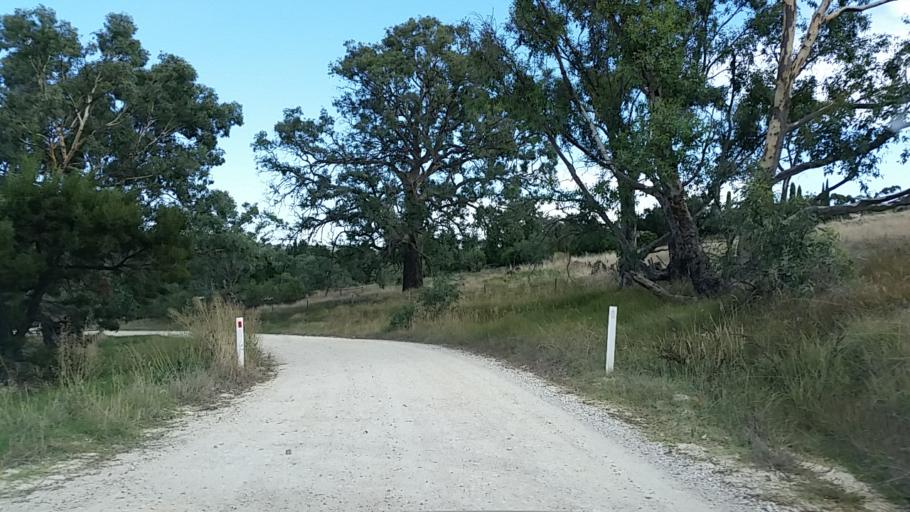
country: AU
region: South Australia
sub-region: Barossa
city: Angaston
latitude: -34.5637
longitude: 139.0790
